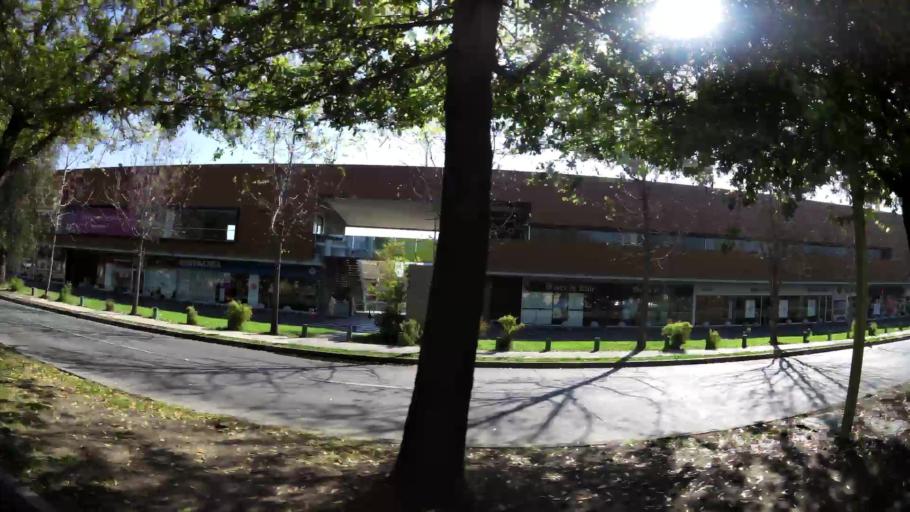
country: CL
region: Santiago Metropolitan
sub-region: Provincia de Santiago
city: Villa Presidente Frei, Nunoa, Santiago, Chile
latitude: -33.4017
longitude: -70.5137
